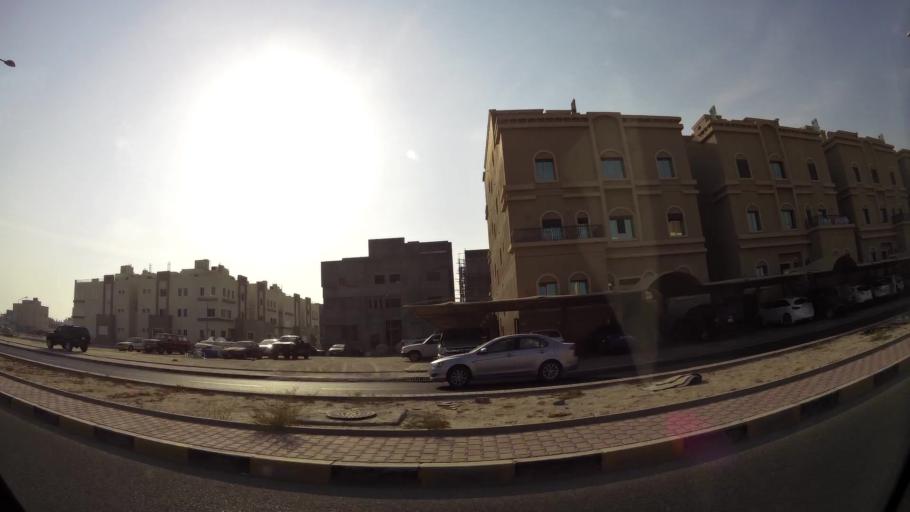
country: KW
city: Al Funaytis
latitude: 29.2049
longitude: 48.1008
